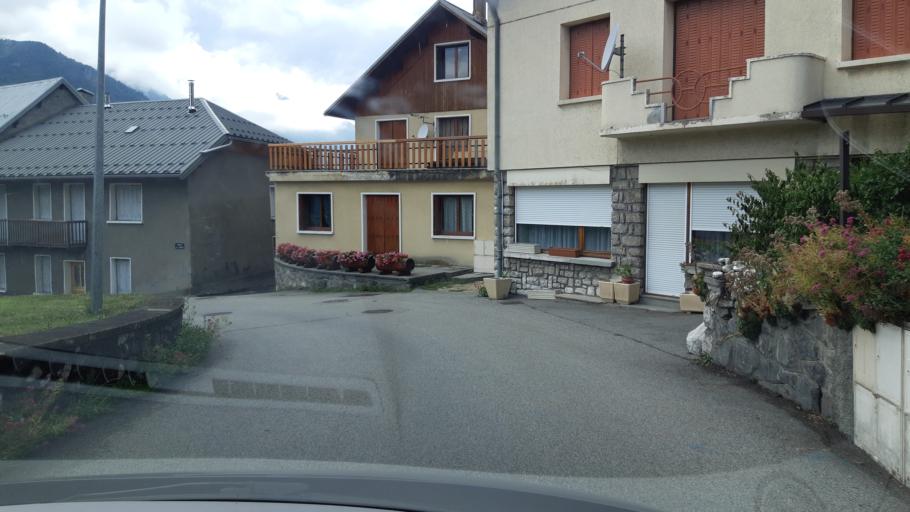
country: FR
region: Rhone-Alpes
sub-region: Departement de la Savoie
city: Saint-Michel-de-Maurienne
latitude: 45.2413
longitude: 6.4455
